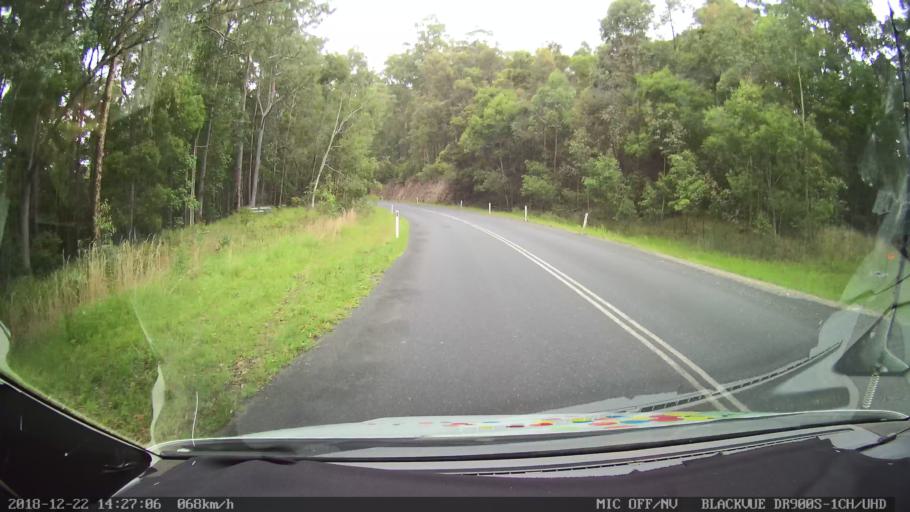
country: AU
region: New South Wales
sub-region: Bellingen
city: Dorrigo
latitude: -30.0619
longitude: 152.6339
